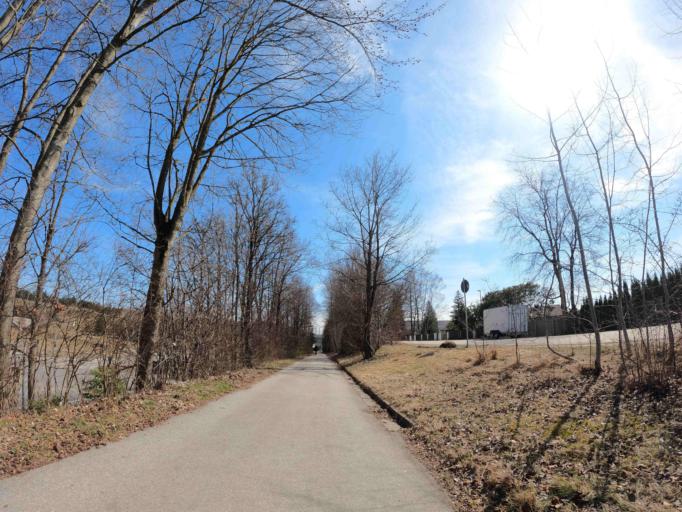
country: DE
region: Bavaria
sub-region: Upper Bavaria
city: Hohenbrunn
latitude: 48.0411
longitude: 11.6779
